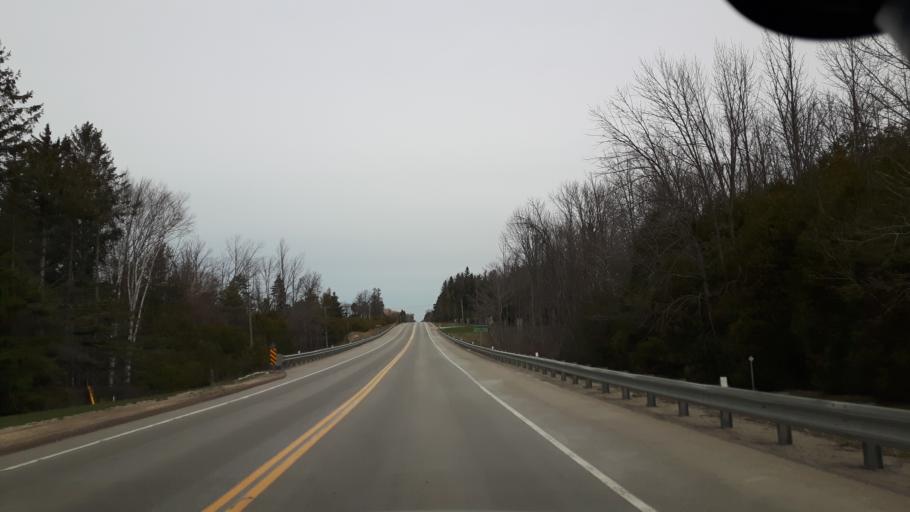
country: CA
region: Ontario
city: Goderich
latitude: 43.6654
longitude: -81.7056
